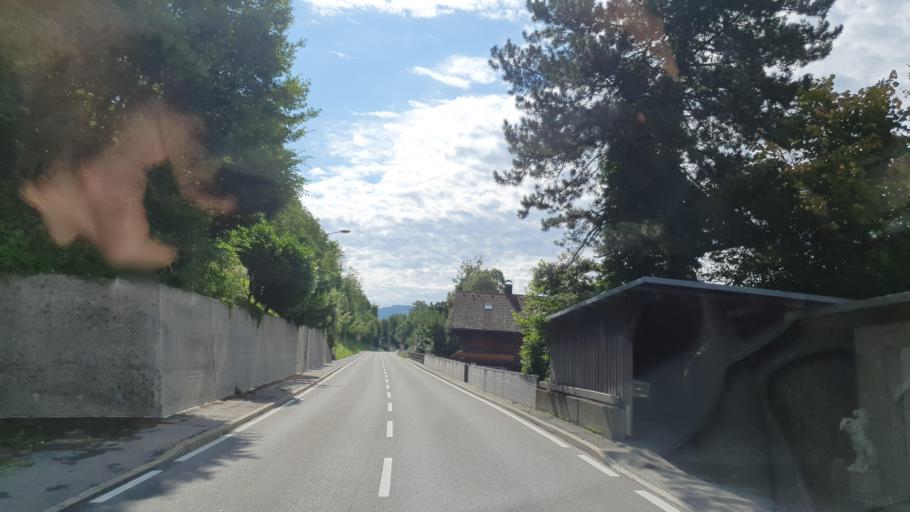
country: AT
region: Vorarlberg
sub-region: Politischer Bezirk Bregenz
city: Kennelbach
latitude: 47.4863
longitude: 9.7517
